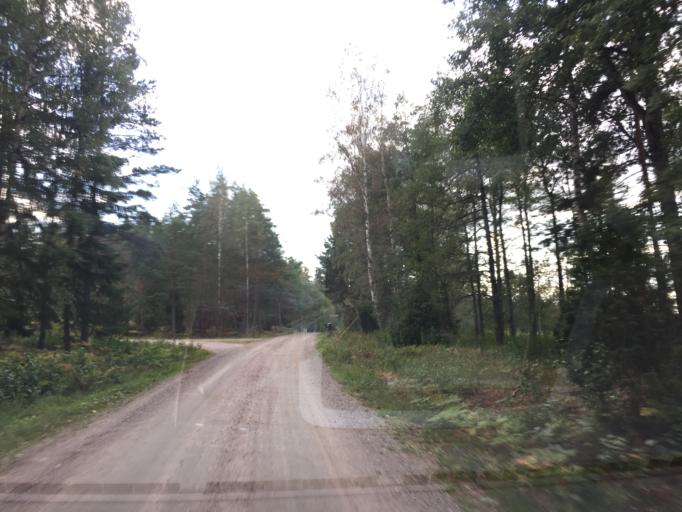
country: SE
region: Soedermanland
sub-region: Vingakers Kommun
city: Vingaker
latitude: 58.9942
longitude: 15.7399
